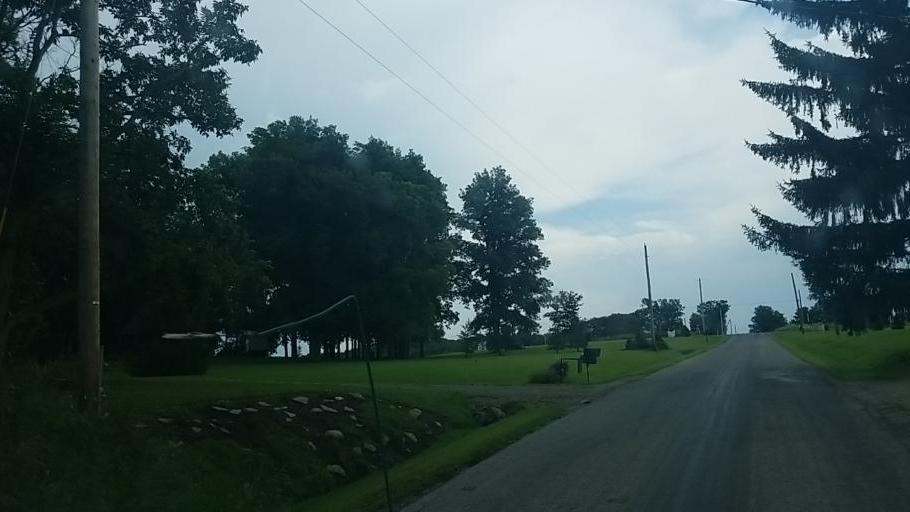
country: US
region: Ohio
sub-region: Wayne County
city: Creston
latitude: 40.9608
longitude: -81.9378
